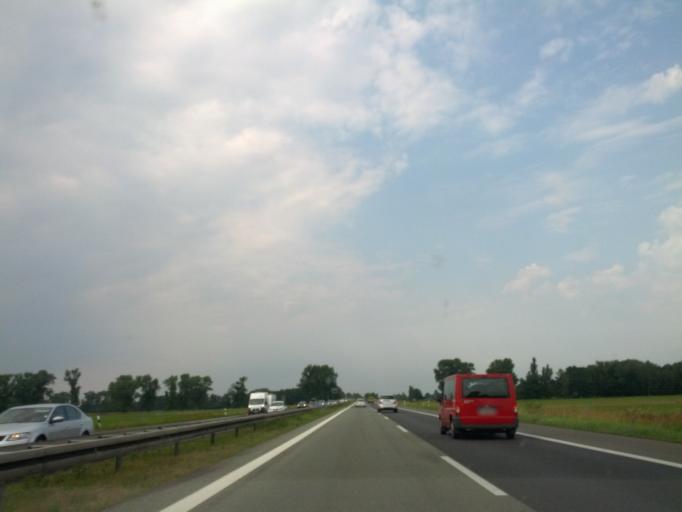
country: DE
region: Brandenburg
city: Fehrbellin
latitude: 52.8140
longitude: 12.7942
